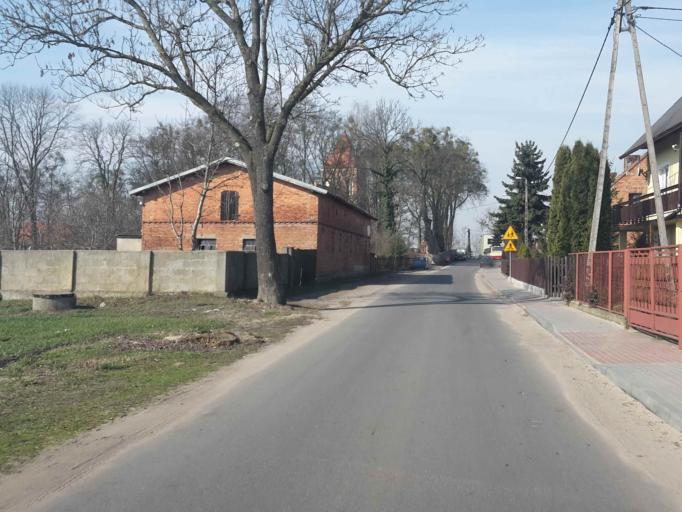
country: PL
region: Kujawsko-Pomorskie
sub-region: Powiat wabrzeski
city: Debowa Laka
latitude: 53.2140
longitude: 19.1758
